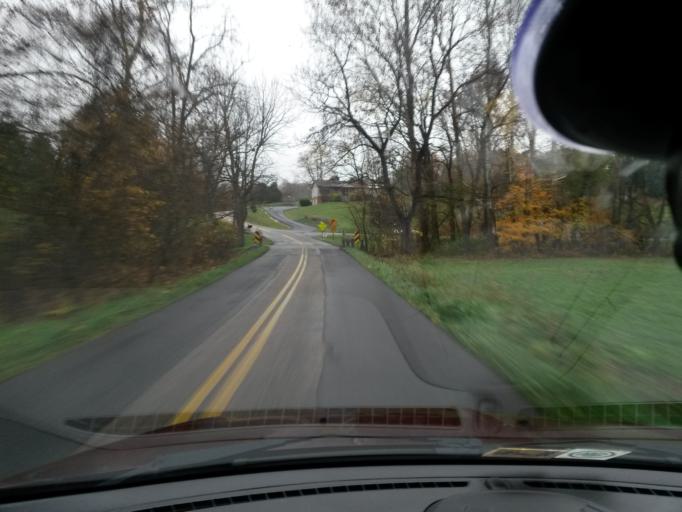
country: US
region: Virginia
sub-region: Botetourt County
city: Fincastle
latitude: 37.4759
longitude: -79.8757
